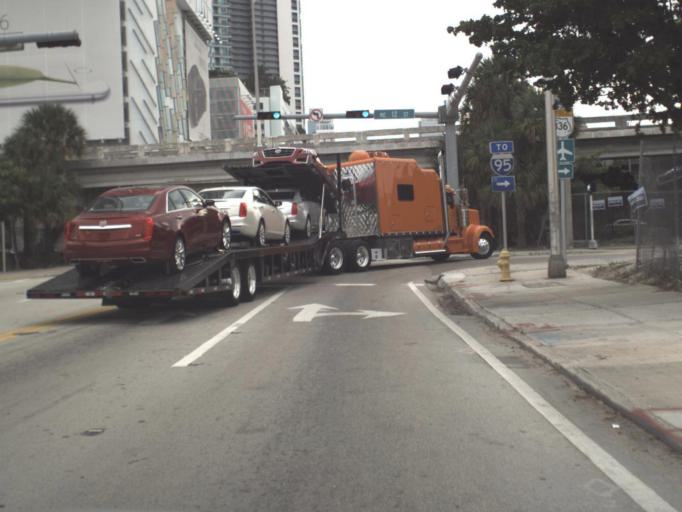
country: US
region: Florida
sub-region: Miami-Dade County
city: Miami
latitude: 25.7864
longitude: -80.1907
